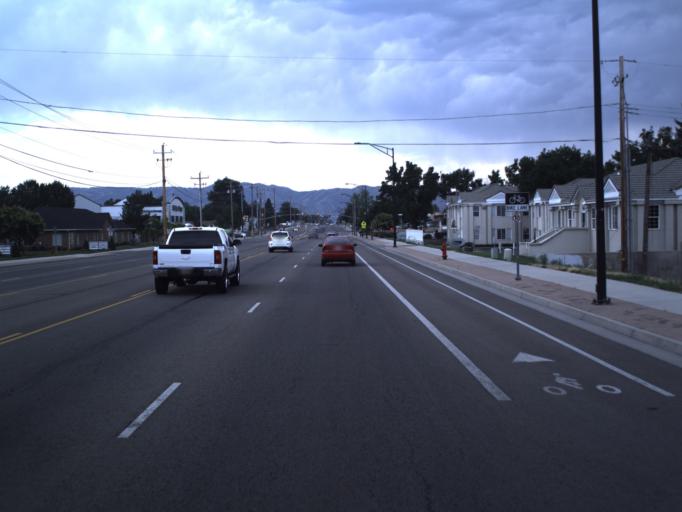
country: US
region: Utah
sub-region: Salt Lake County
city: White City
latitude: 40.5765
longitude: -111.8723
